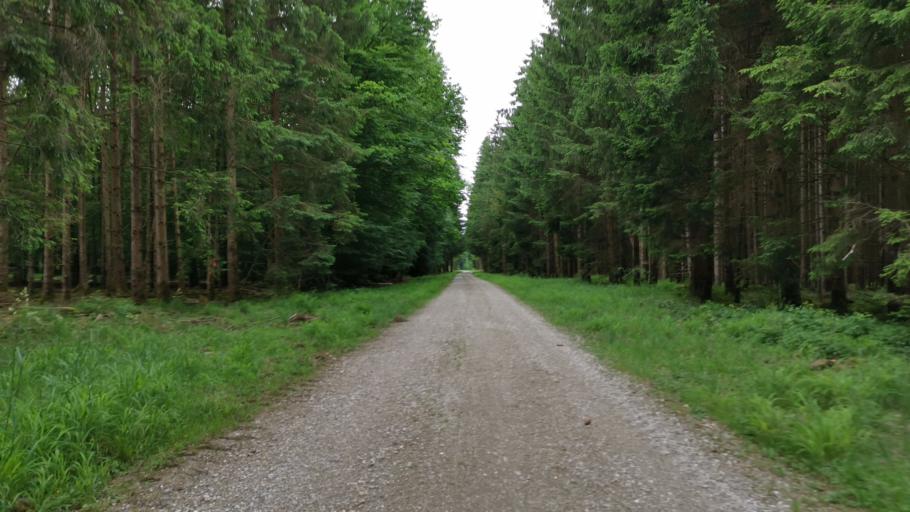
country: DE
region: Bavaria
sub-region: Upper Bavaria
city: Baierbrunn
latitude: 48.0496
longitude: 11.4920
